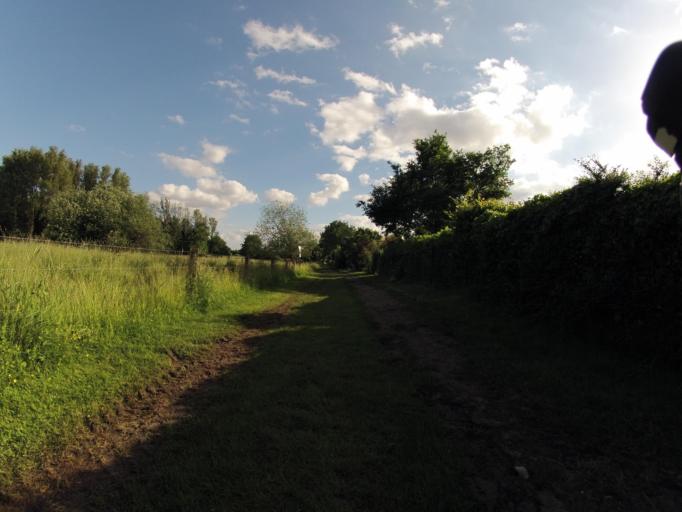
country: DE
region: North Rhine-Westphalia
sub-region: Regierungsbezirk Munster
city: Horstel
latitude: 52.2748
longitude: 7.5957
